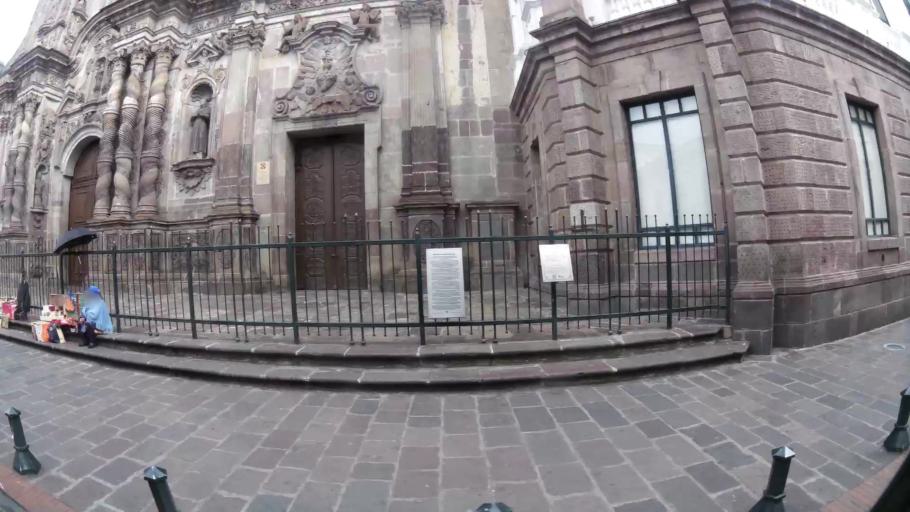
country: EC
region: Pichincha
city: Quito
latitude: -0.2210
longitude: -78.5135
